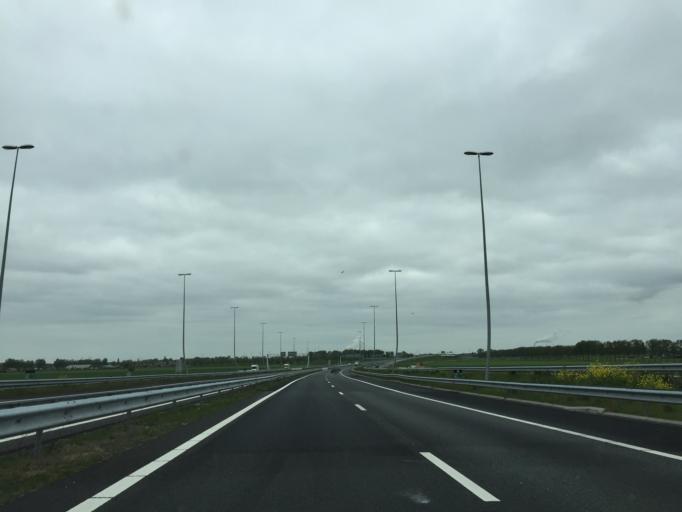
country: NL
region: North Holland
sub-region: Gemeente Haarlemmermeer
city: Hoofddorp
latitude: 52.3597
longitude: 4.7427
